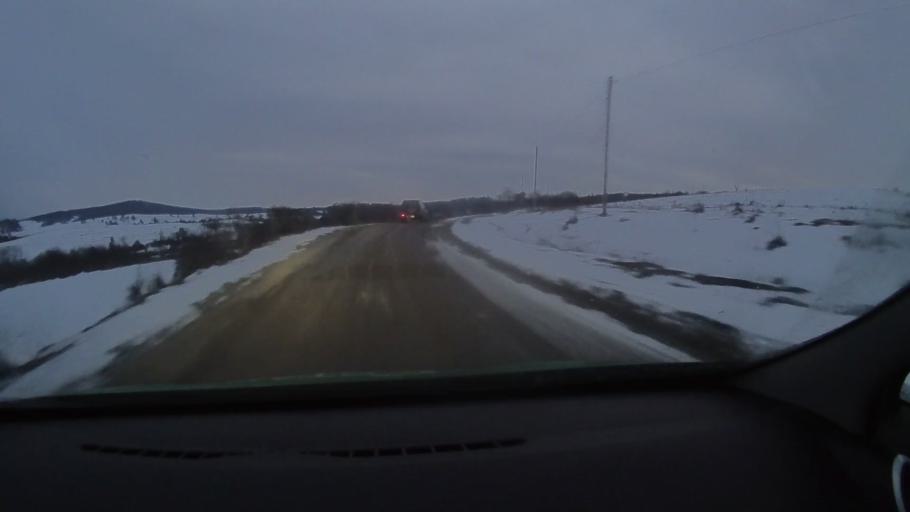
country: RO
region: Harghita
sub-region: Comuna Darjiu
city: Darjiu
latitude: 46.1915
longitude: 25.2465
